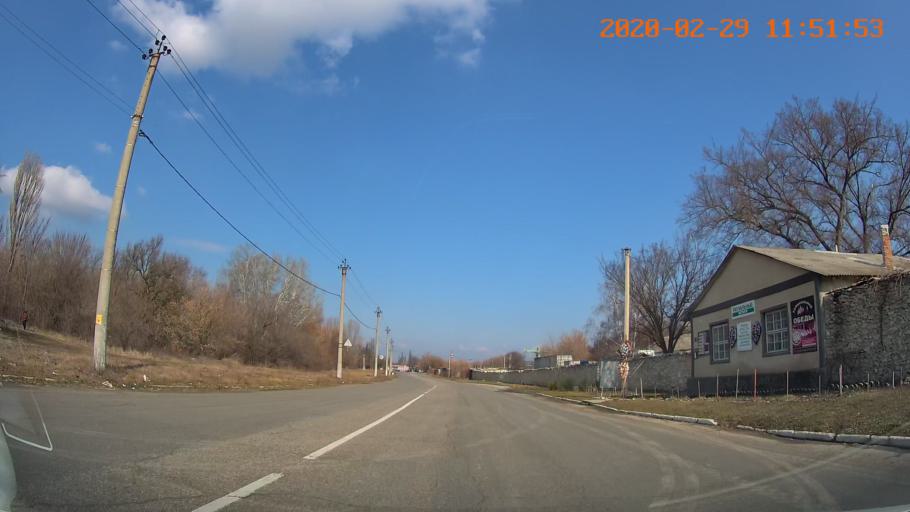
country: MD
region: Telenesti
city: Ribnita
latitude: 47.7675
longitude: 28.9910
